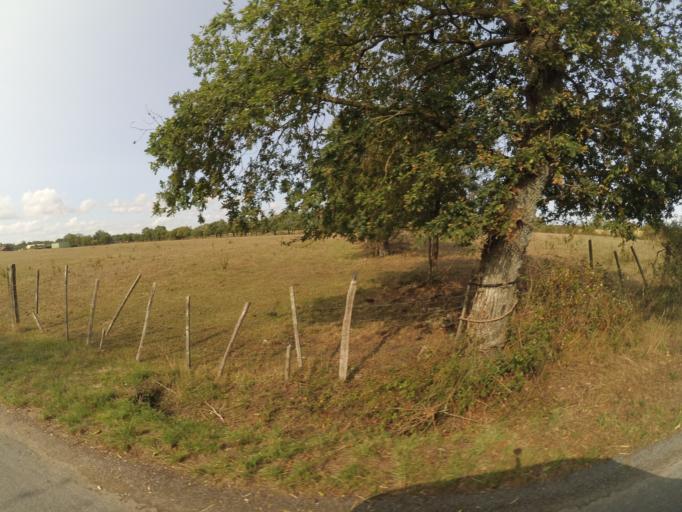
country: FR
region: Pays de la Loire
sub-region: Departement de la Vendee
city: La Bruffiere
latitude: 46.9938
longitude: -1.1926
